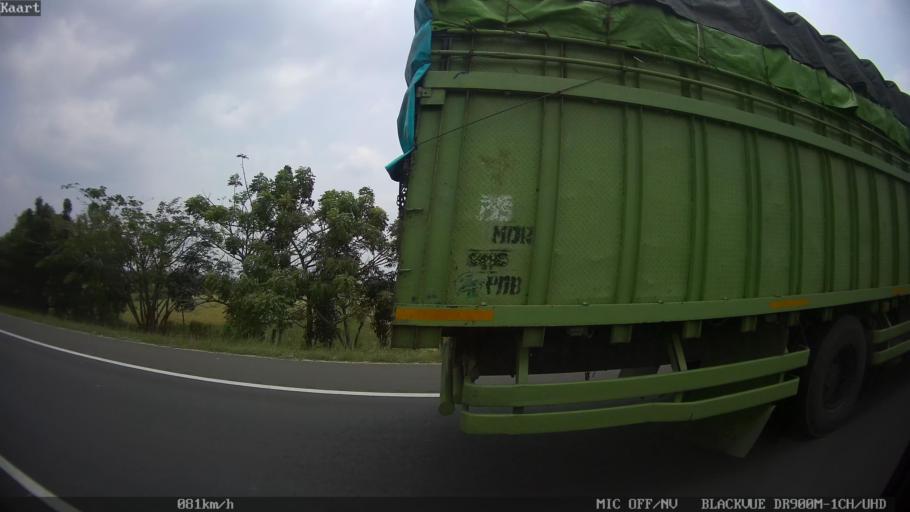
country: ID
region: Banten
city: Bojonegara
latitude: -6.0102
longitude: 106.0739
